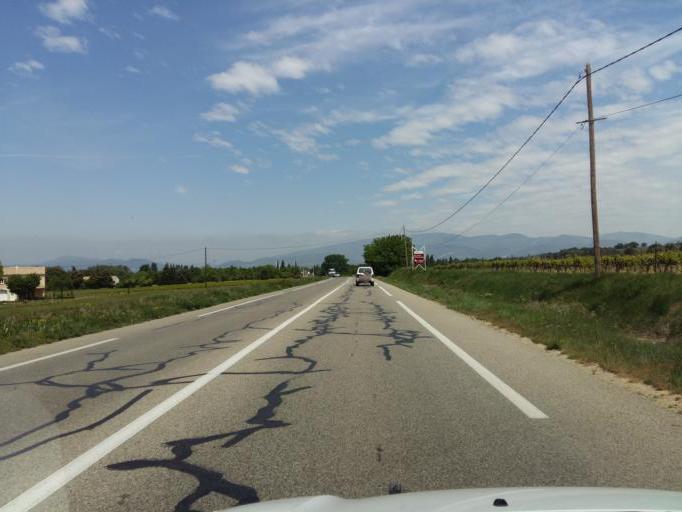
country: FR
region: Provence-Alpes-Cote d'Azur
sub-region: Departement du Vaucluse
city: Valreas
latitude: 44.3602
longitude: 4.9715
